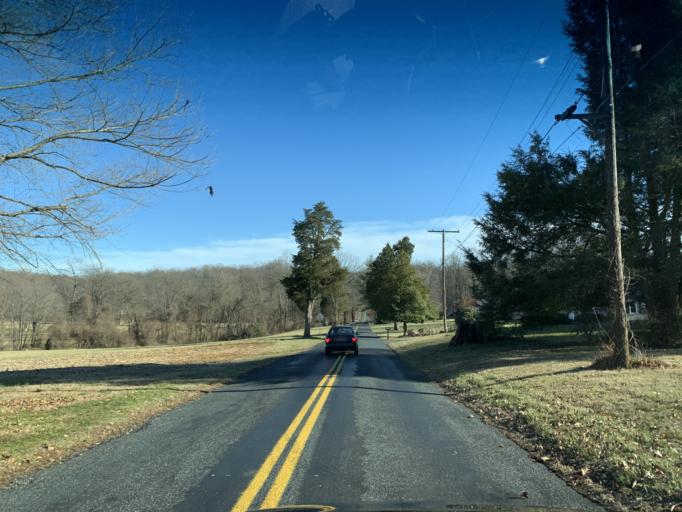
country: US
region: Maryland
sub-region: Harford County
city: Riverside
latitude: 39.5450
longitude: -76.2508
